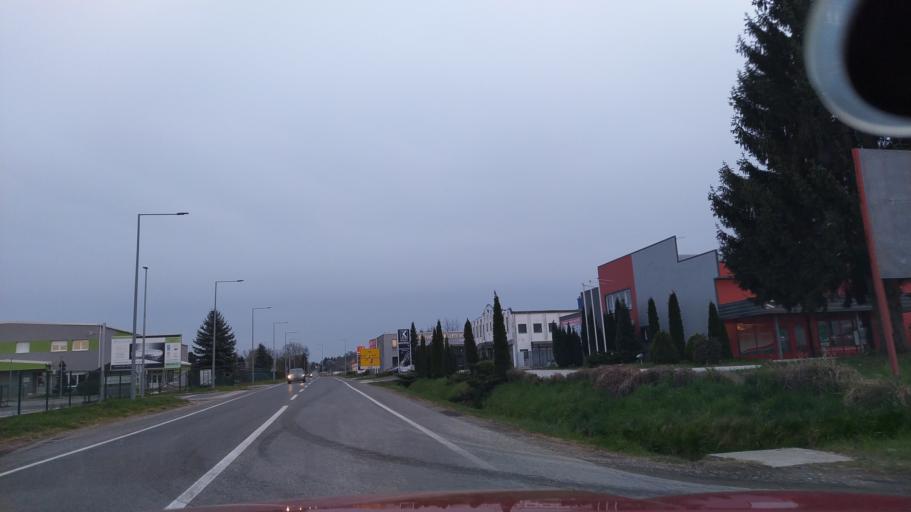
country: HR
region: Varazdinska
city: Ludbreg
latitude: 46.2432
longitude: 16.6261
